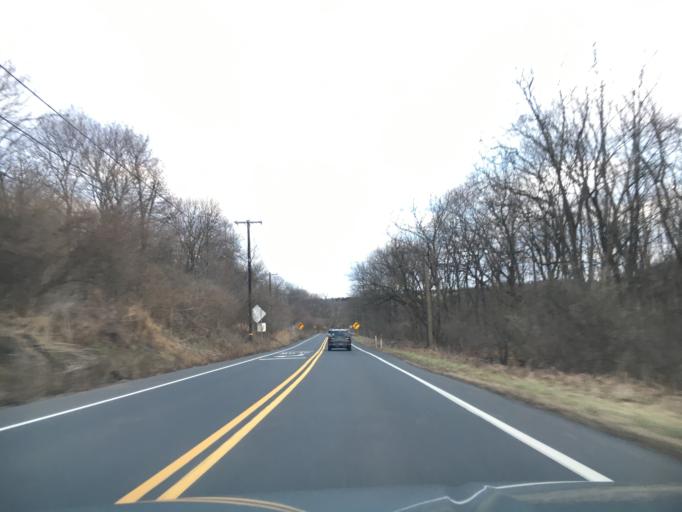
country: US
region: Pennsylvania
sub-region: Lehigh County
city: Schnecksville
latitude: 40.6788
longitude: -75.6495
